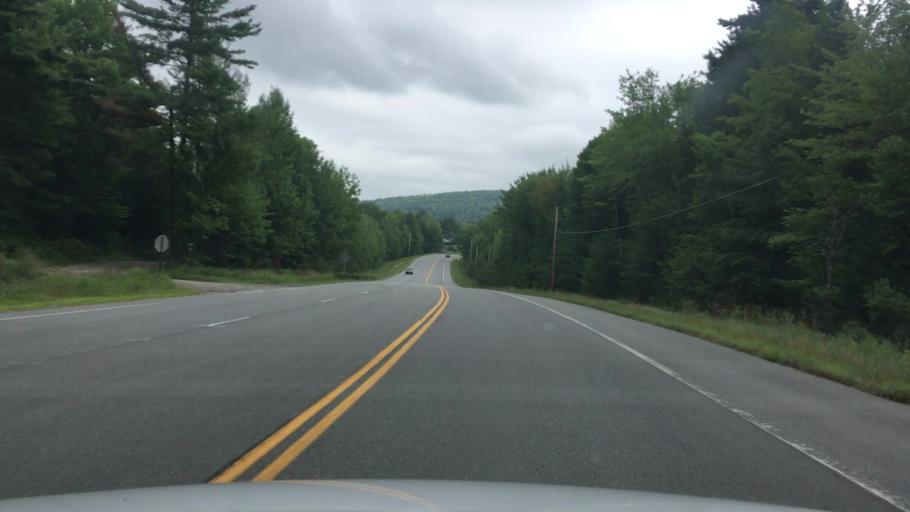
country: US
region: Maine
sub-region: Penobscot County
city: Bradley
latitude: 44.8213
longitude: -68.4961
